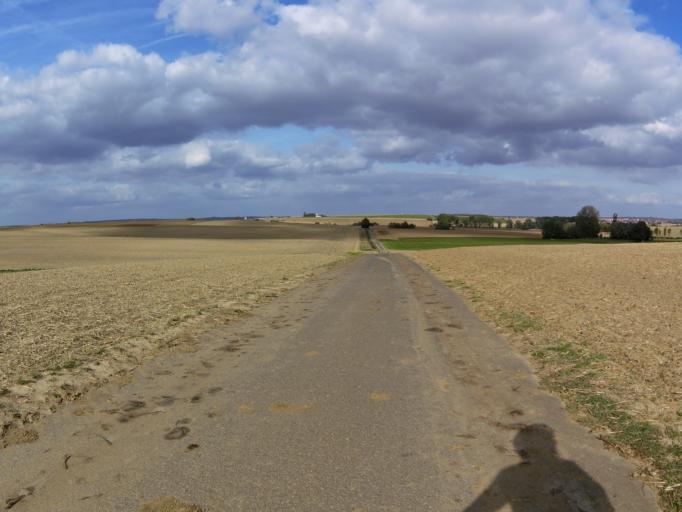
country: DE
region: Bavaria
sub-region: Regierungsbezirk Unterfranken
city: Giebelstadt
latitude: 49.6959
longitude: 9.9457
